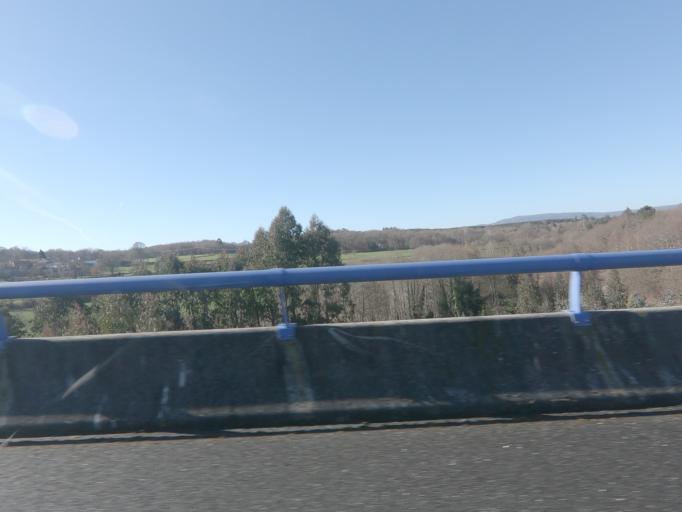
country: ES
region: Galicia
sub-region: Provincia de Pontevedra
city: Lalin
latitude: 42.6295
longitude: -8.1194
